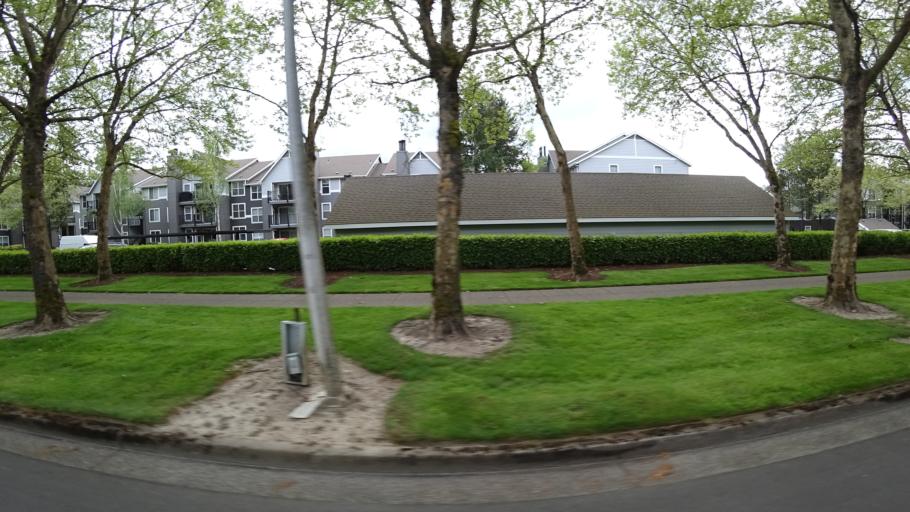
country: US
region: Oregon
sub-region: Washington County
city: Rockcreek
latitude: 45.5443
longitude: -122.8836
